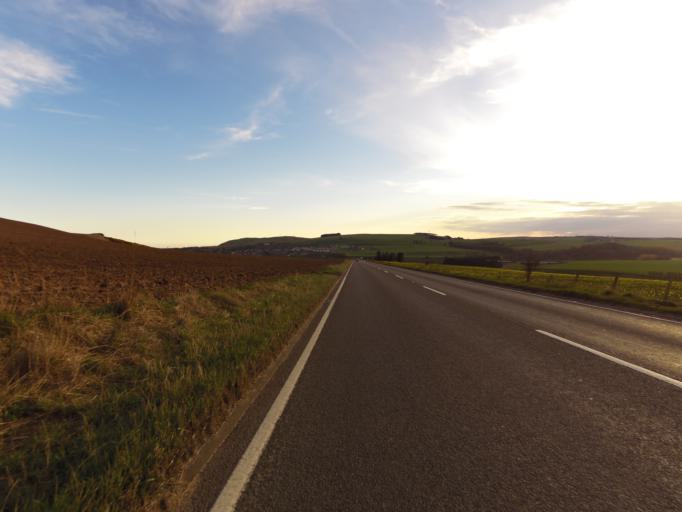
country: GB
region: Scotland
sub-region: Aberdeenshire
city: Inverbervie
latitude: 56.8534
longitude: -2.2734
